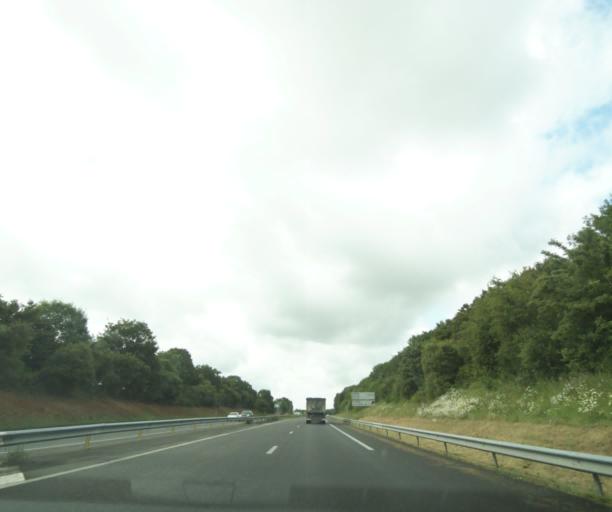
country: FR
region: Pays de la Loire
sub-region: Departement de Maine-et-Loire
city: Durtal
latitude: 47.6792
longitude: -0.2543
